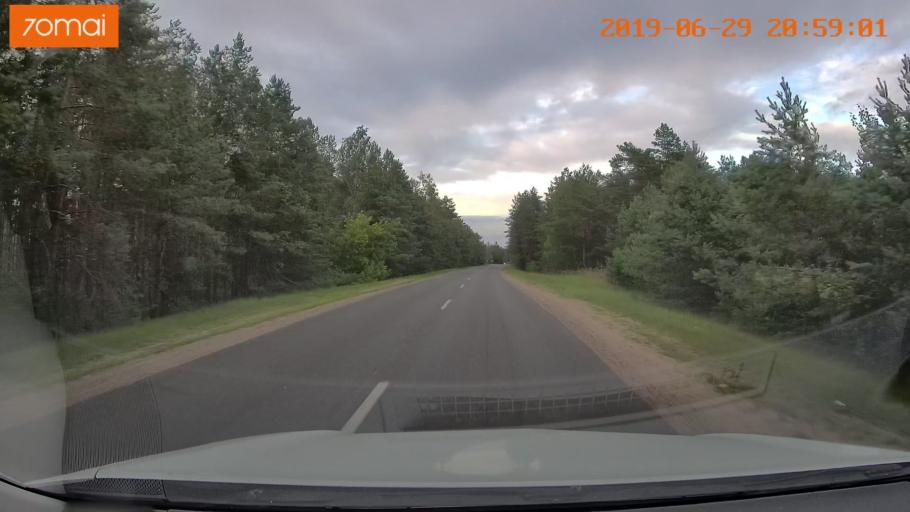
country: BY
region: Brest
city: Hantsavichy
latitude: 52.7345
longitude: 26.3974
